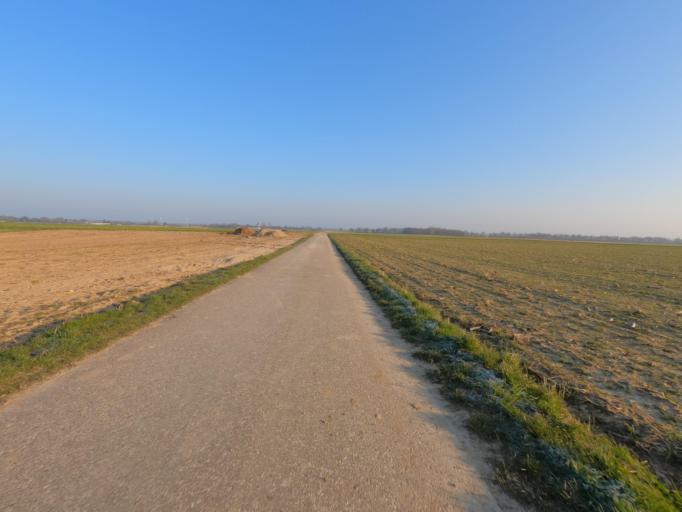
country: DE
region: North Rhine-Westphalia
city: Huckelhoven
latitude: 51.0744
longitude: 6.2621
